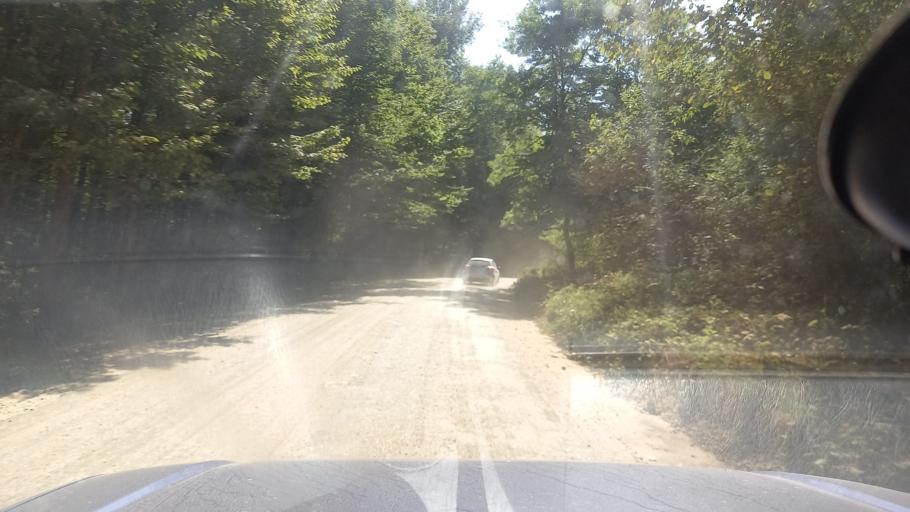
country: RU
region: Krasnodarskiy
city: Azovskaya
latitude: 44.6849
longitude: 38.6385
